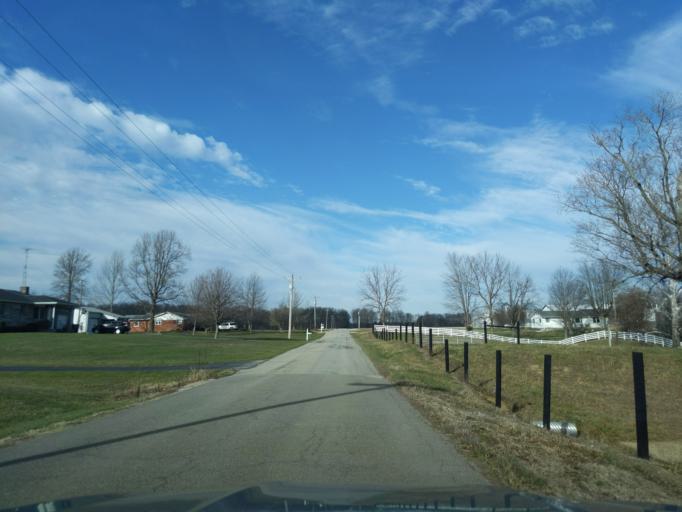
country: US
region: Indiana
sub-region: Decatur County
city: Greensburg
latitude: 39.2740
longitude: -85.4234
